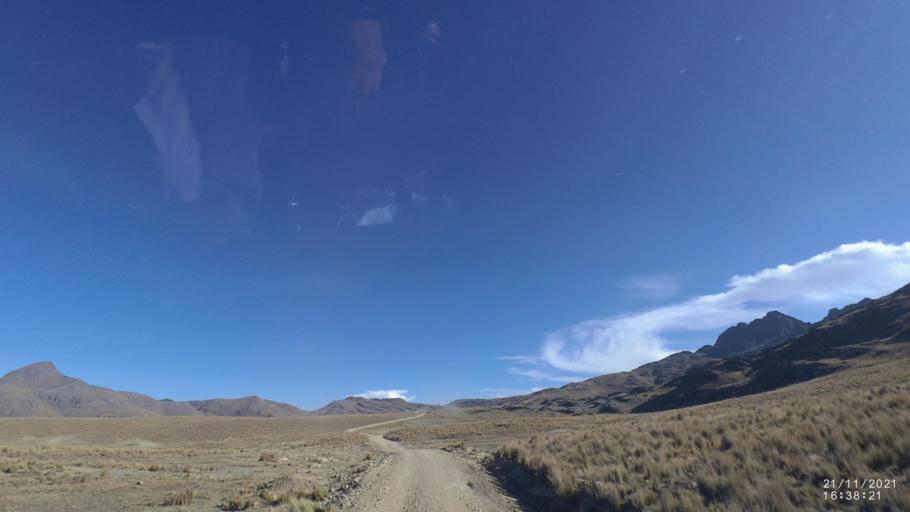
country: BO
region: Cochabamba
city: Cochabamba
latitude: -17.0509
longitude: -66.2626
